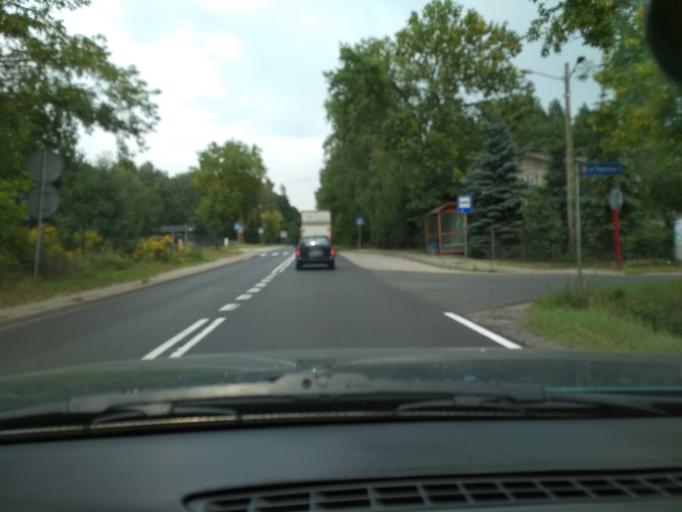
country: PL
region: Silesian Voivodeship
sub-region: Powiat zawiercianski
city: Zawiercie
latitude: 50.4628
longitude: 19.3919
